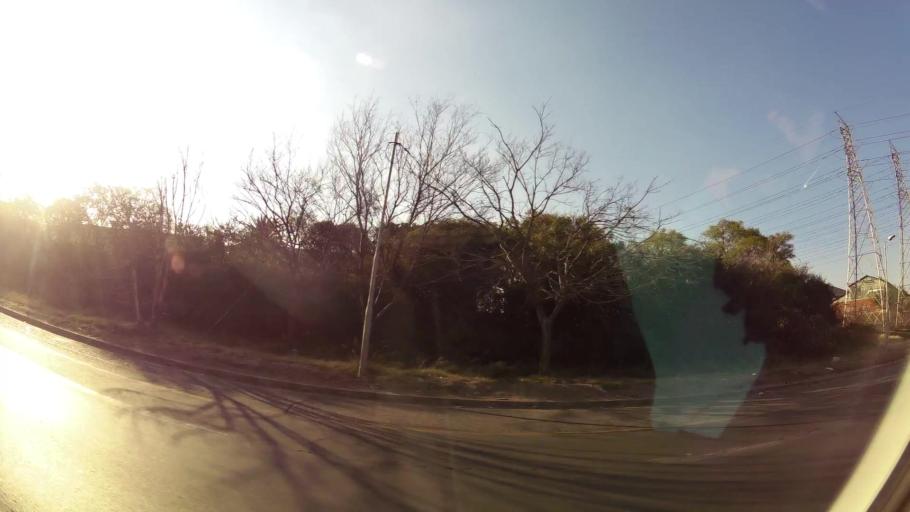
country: ZA
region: Gauteng
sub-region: City of Johannesburg Metropolitan Municipality
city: Johannesburg
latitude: -26.2124
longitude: 28.0720
